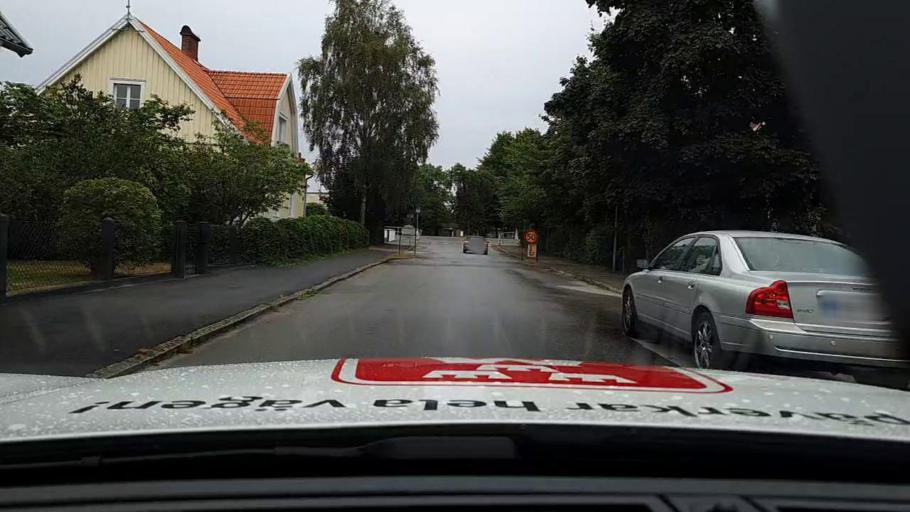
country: SE
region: Skane
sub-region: Hassleholms Kommun
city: Hassleholm
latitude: 56.1642
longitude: 13.7743
